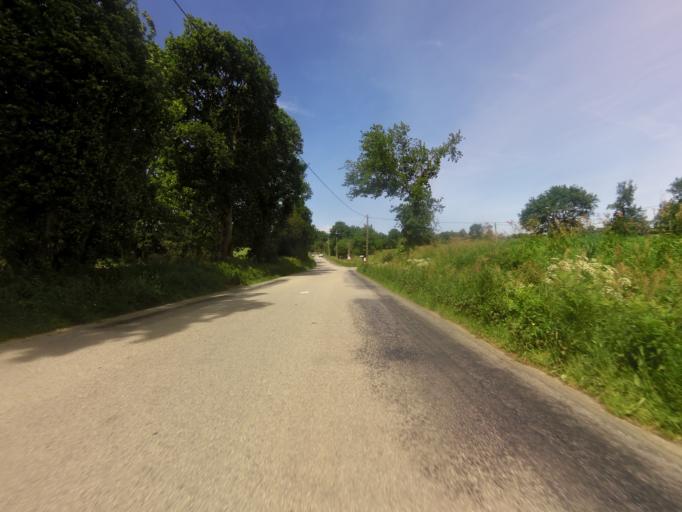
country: FR
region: Brittany
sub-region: Departement du Morbihan
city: Sulniac
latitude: 47.6864
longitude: -2.5717
